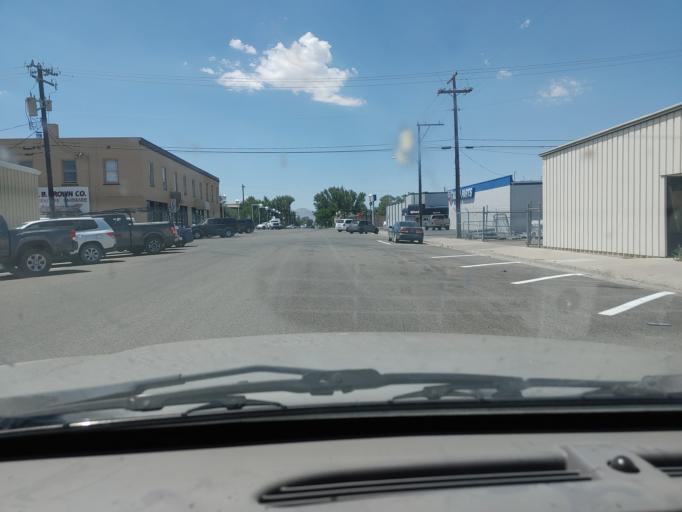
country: US
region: Nevada
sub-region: Humboldt County
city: Winnemucca
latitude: 40.9750
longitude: -117.7352
